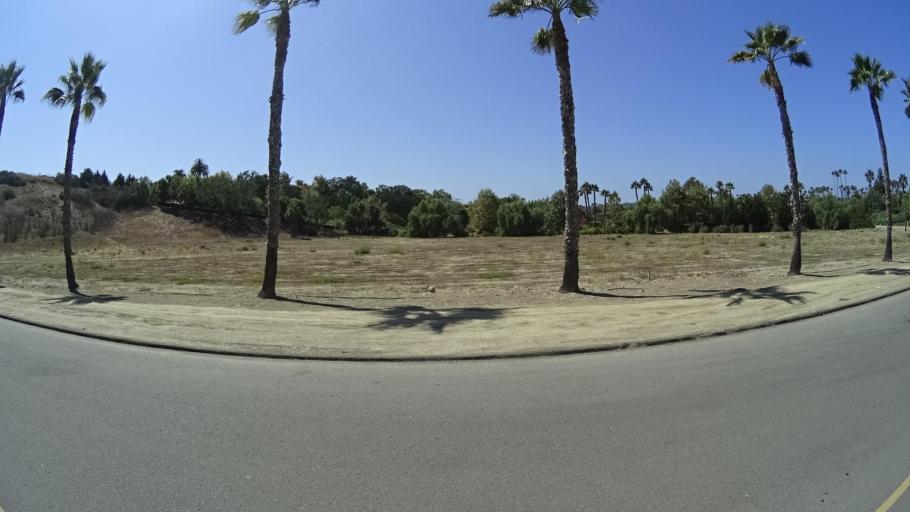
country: US
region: California
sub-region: San Diego County
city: Fairbanks Ranch
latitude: 32.9911
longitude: -117.1915
